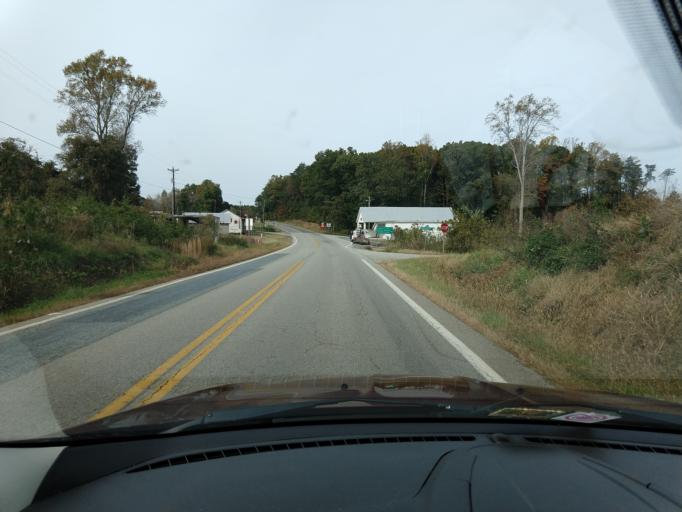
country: US
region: Virginia
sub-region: Franklin County
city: Union Hall
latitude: 36.9556
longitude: -79.5344
